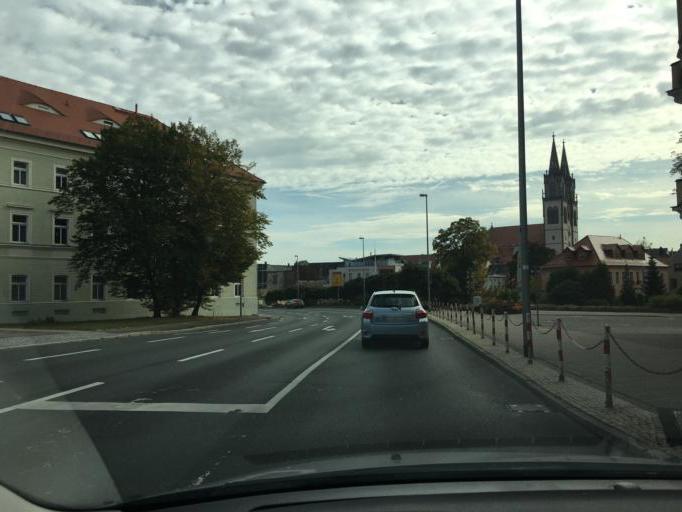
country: DE
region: Saxony
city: Oschatz
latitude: 51.3001
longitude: 13.1049
